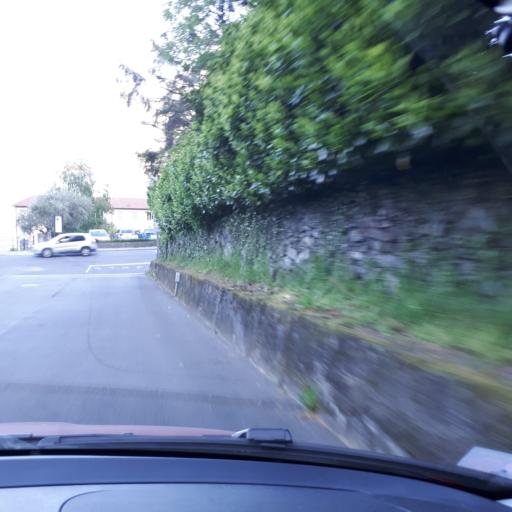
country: IT
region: Lombardy
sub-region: Provincia di Como
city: Musso
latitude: 46.1115
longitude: 9.2761
